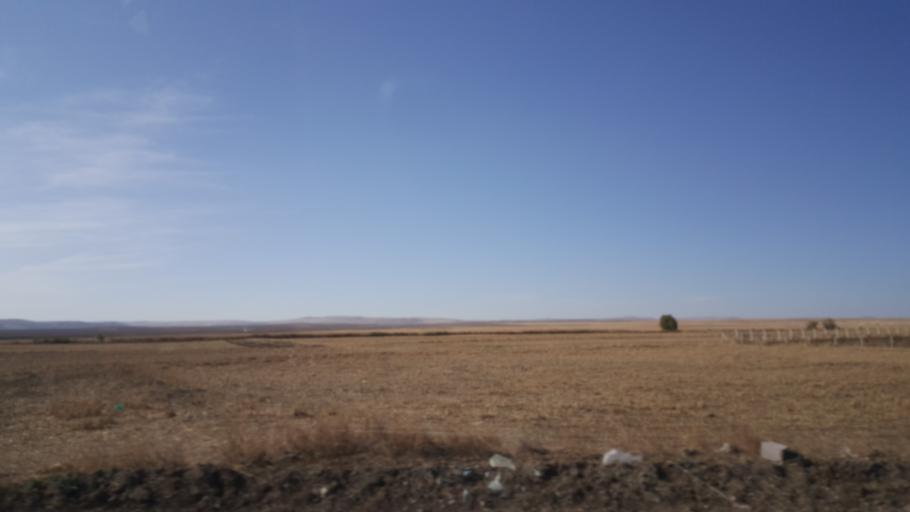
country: TR
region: Ankara
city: Yenice
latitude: 39.3704
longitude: 32.8114
